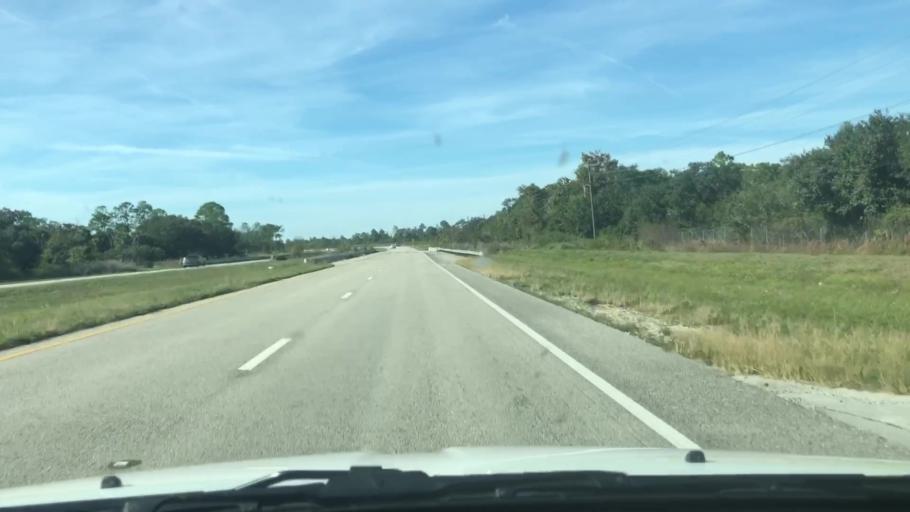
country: US
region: Florida
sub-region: Indian River County
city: Fellsmere
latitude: 27.6875
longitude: -80.8789
